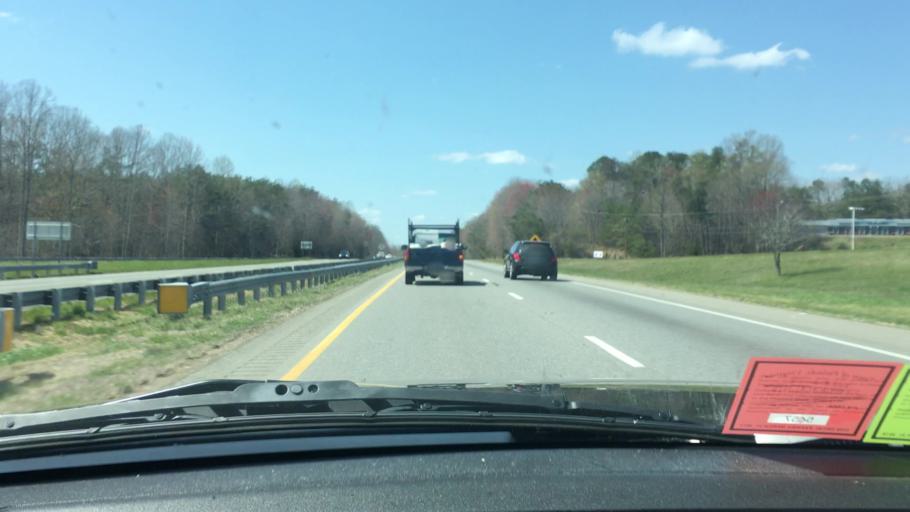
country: US
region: North Carolina
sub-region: Surry County
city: Pilot Mountain
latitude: 36.4088
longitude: -80.4997
